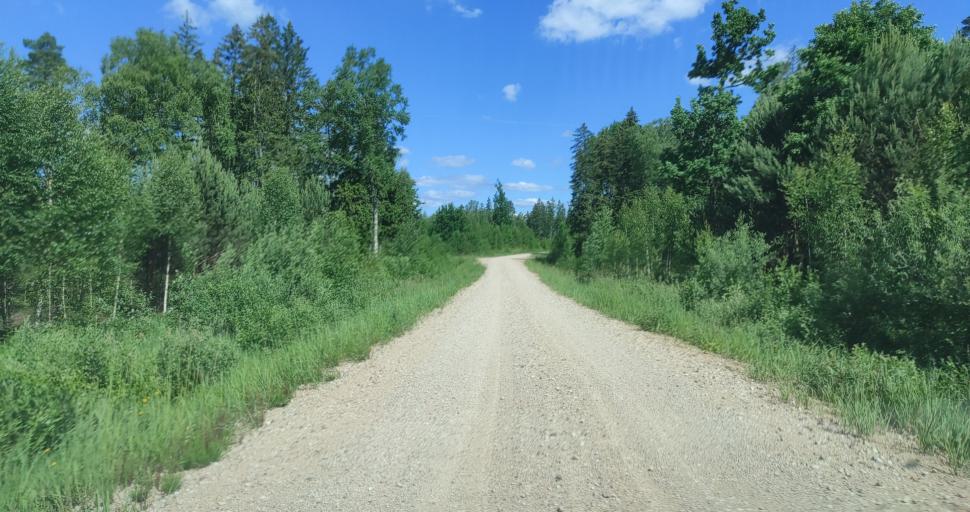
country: LV
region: Kuldigas Rajons
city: Kuldiga
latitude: 56.9294
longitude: 21.7971
